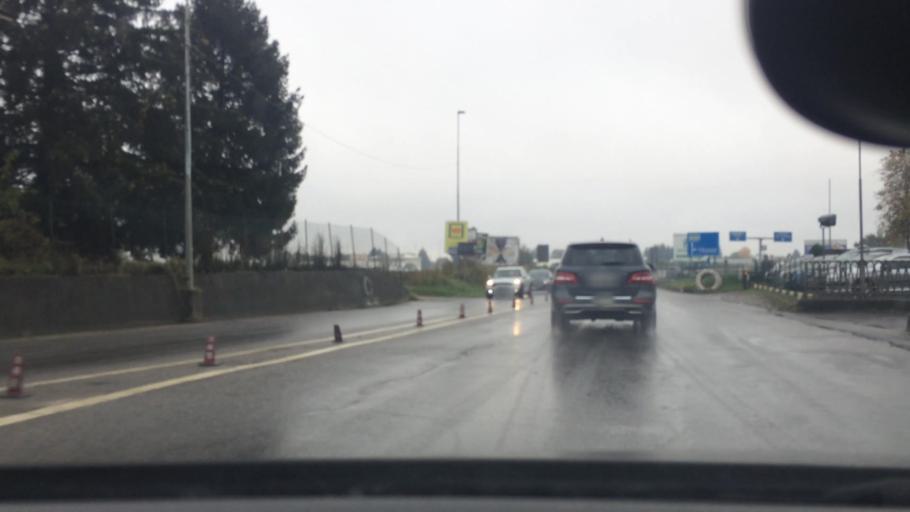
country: IT
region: Lombardy
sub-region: Provincia di Como
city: Carimate
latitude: 45.6966
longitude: 9.0975
